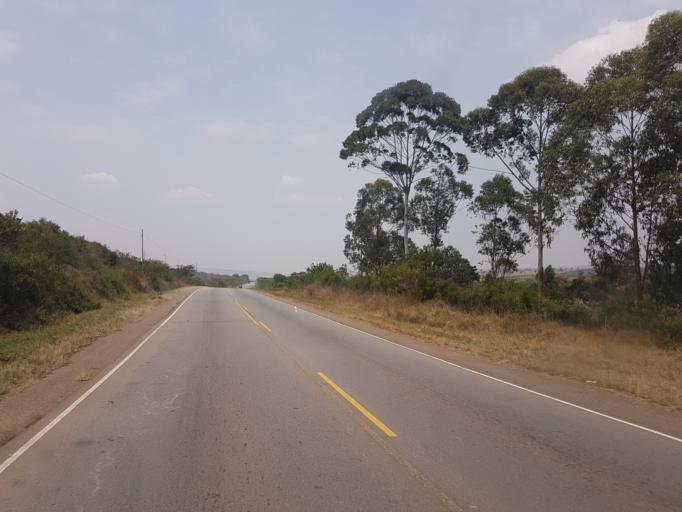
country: UG
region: Western Region
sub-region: Mbarara District
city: Mbarara
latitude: -0.5105
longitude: 30.7906
